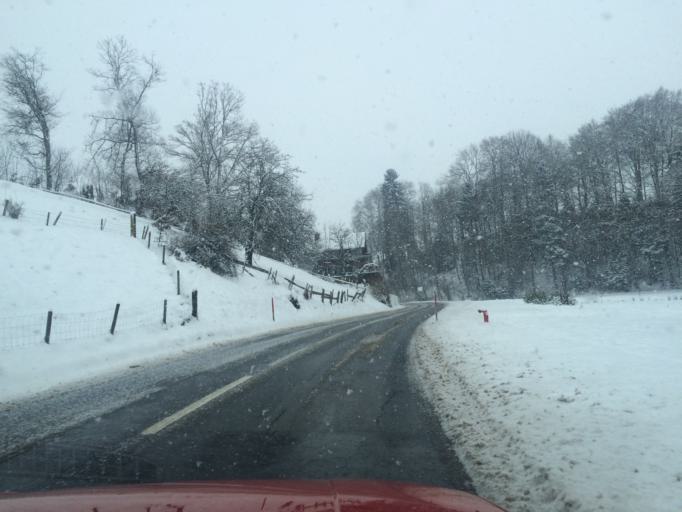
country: CH
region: Bern
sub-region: Bern-Mittelland District
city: Toffen
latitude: 46.8669
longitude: 7.4512
